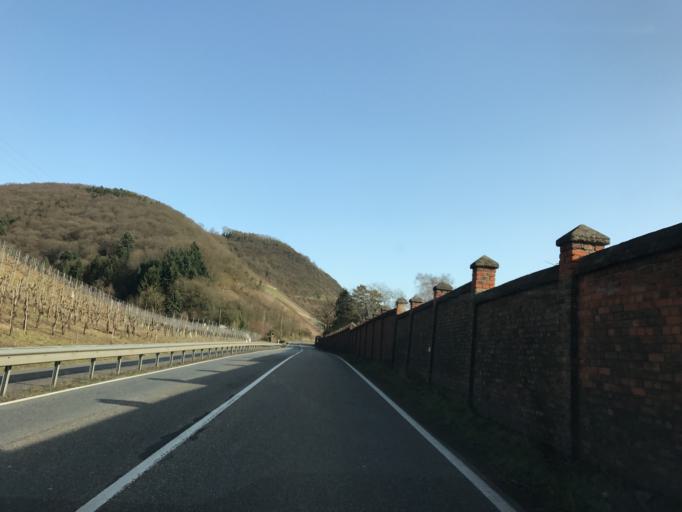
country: DE
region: Rheinland-Pfalz
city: Hammerstein
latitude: 50.4659
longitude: 7.3633
